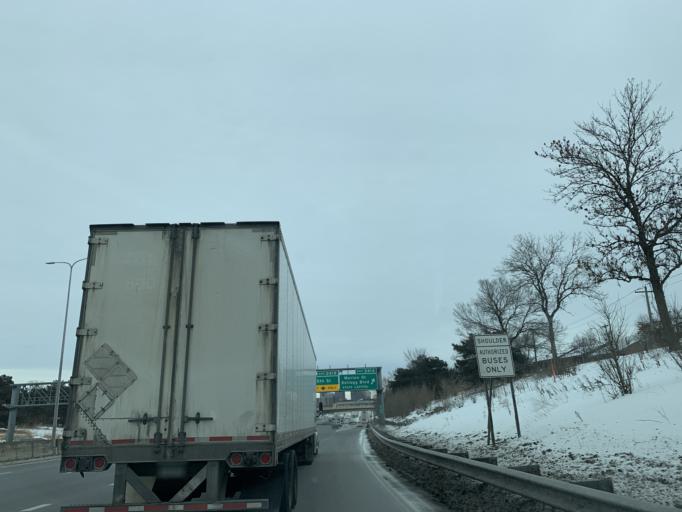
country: US
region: Minnesota
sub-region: Ramsey County
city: Saint Paul
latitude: 44.9513
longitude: -93.1199
